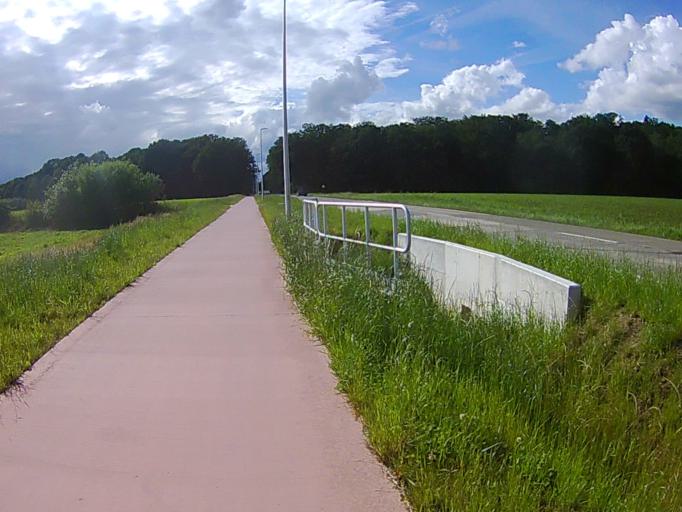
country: BE
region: Flanders
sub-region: Provincie Antwerpen
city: Berlaar
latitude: 51.1293
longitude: 4.6462
